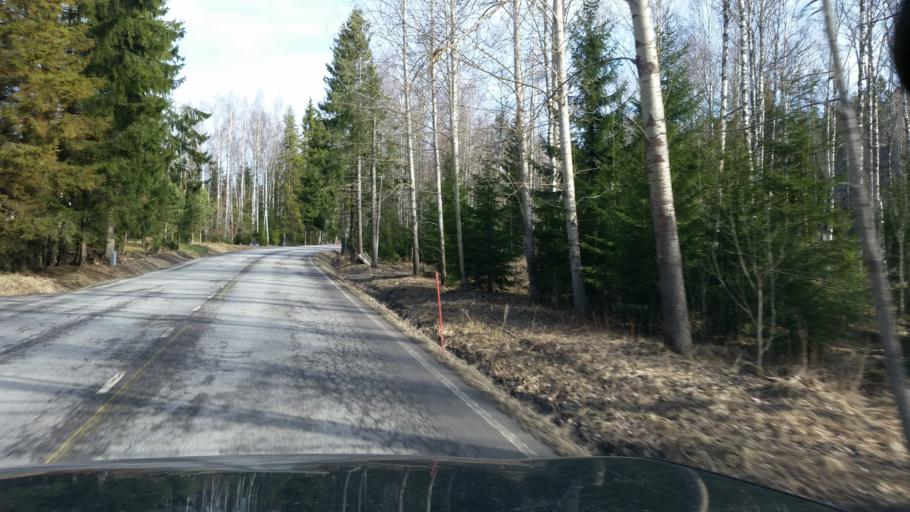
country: FI
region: Uusimaa
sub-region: Helsinki
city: Kirkkonummi
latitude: 60.0989
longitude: 24.3647
